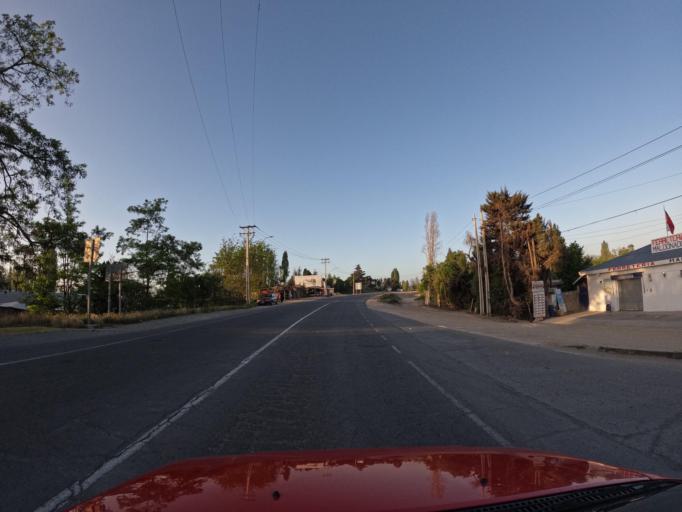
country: CL
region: O'Higgins
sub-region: Provincia de Cachapoal
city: San Vicente
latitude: -34.1673
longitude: -71.3965
